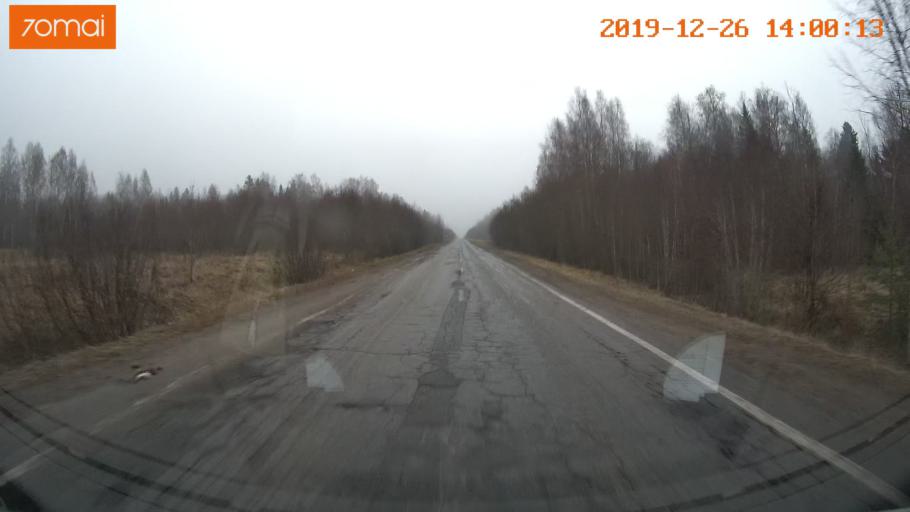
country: RU
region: Jaroslavl
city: Poshekhon'ye
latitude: 58.5597
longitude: 38.7392
